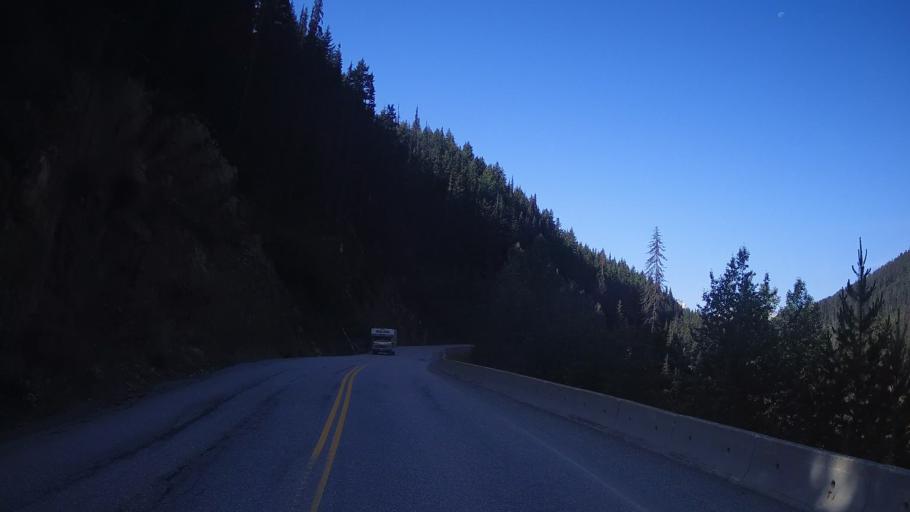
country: CA
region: British Columbia
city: Lillooet
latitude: 50.4312
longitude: -122.2604
